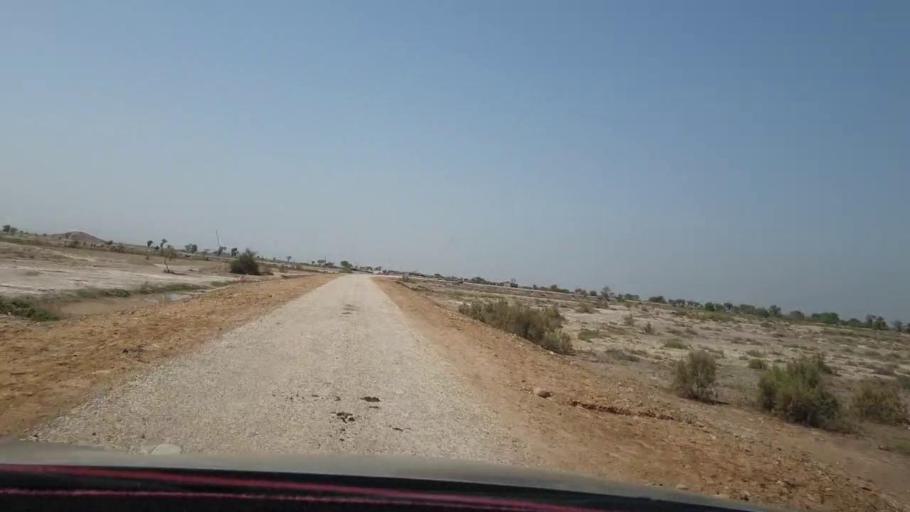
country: PK
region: Sindh
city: Warah
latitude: 27.5049
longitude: 67.7069
